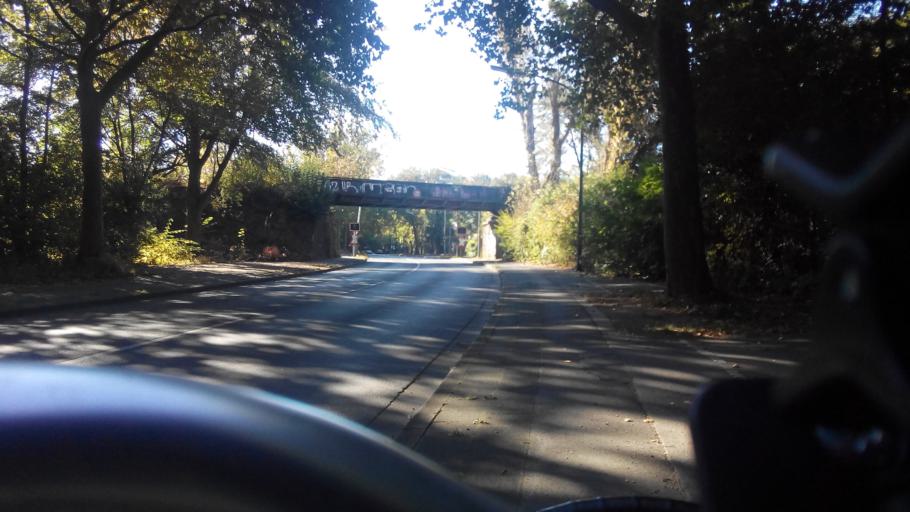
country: DE
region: North Rhine-Westphalia
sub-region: Regierungsbezirk Munster
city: Gelsenkirchen
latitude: 51.5122
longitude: 7.1369
